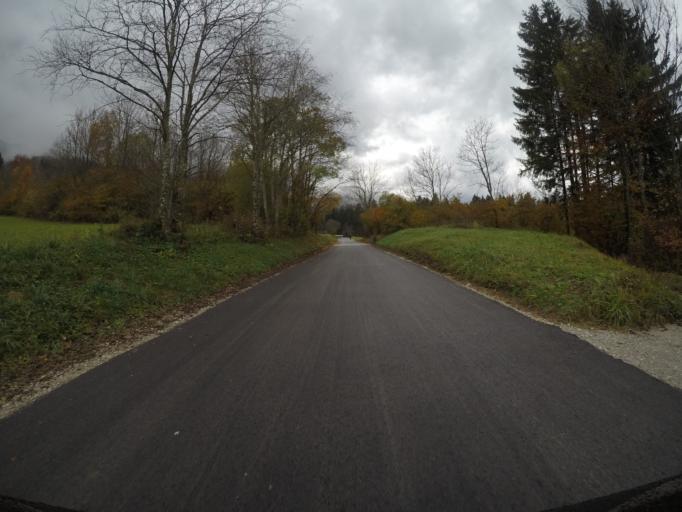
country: SI
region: Kranjska Gora
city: Kranjska Gora
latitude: 46.4907
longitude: 13.7387
